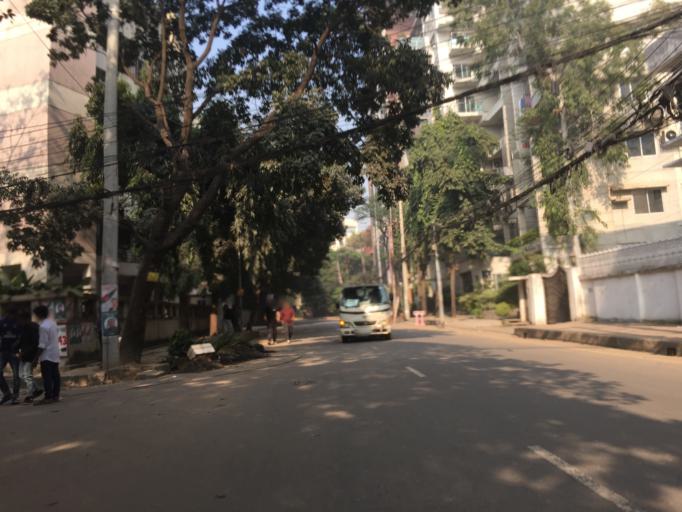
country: BD
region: Dhaka
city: Paltan
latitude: 23.7940
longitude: 90.4197
